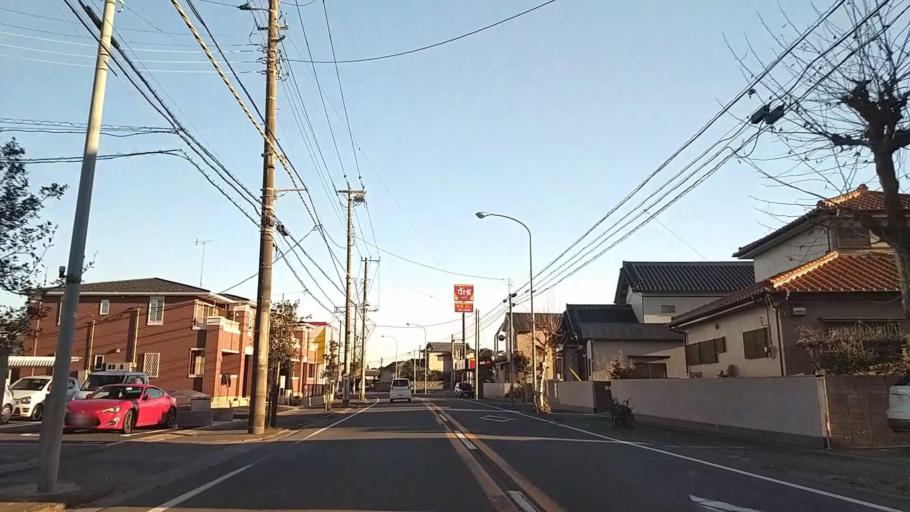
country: JP
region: Chiba
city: Hasaki
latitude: 35.7371
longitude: 140.8039
